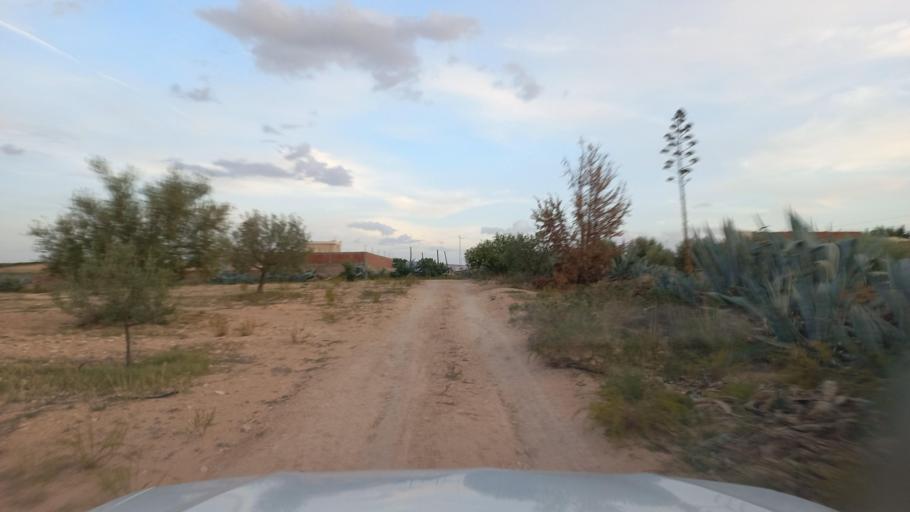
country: TN
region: Al Qasrayn
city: Sbiba
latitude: 35.4104
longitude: 9.1044
